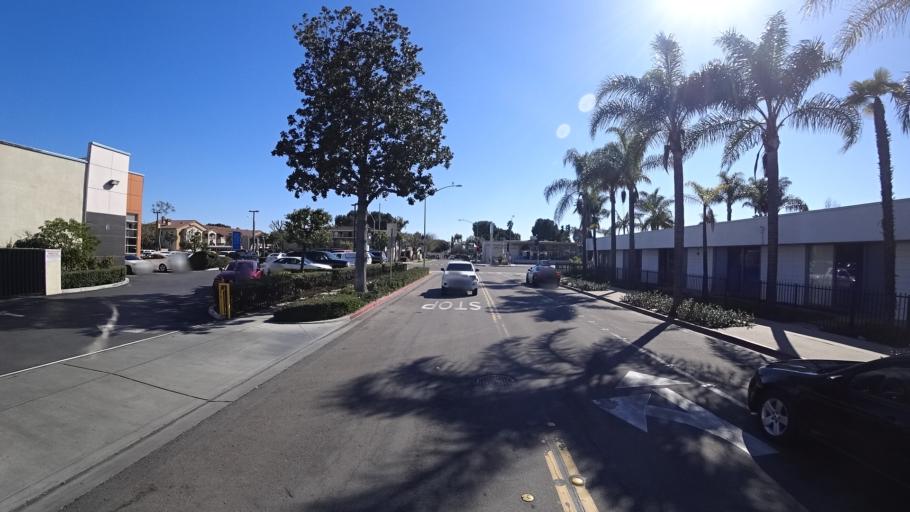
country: US
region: California
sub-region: Orange County
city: Stanton
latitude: 33.8330
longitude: -117.9624
